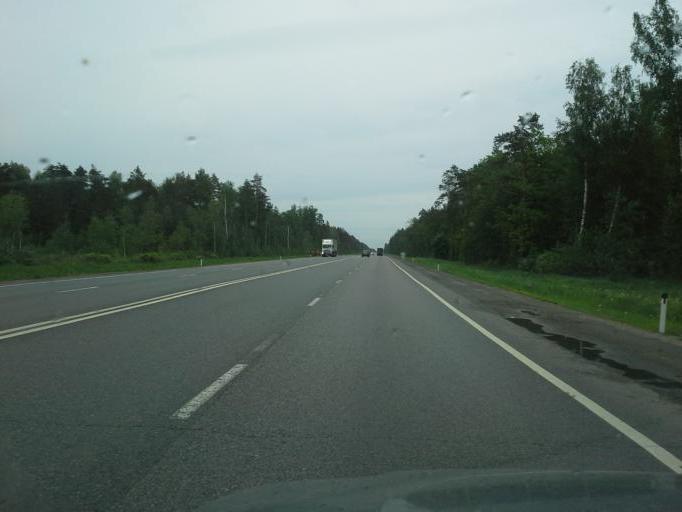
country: RU
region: Vladimir
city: Pokrov
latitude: 55.9071
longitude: 39.1052
